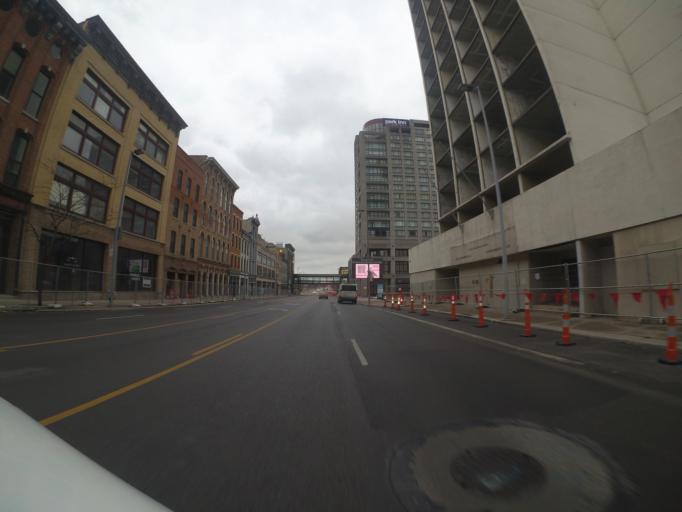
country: US
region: Ohio
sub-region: Lucas County
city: Toledo
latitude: 41.6494
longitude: -83.5352
